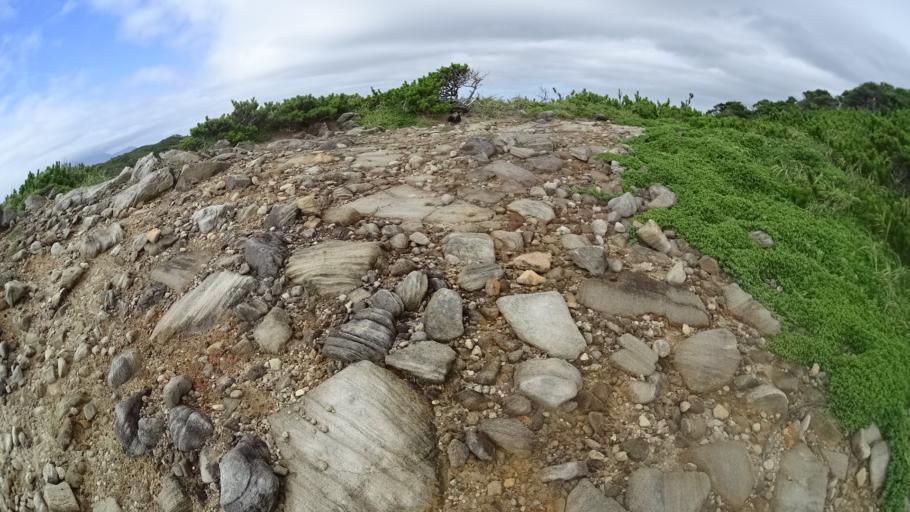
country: JP
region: Shizuoka
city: Shimoda
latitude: 34.3256
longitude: 139.2030
